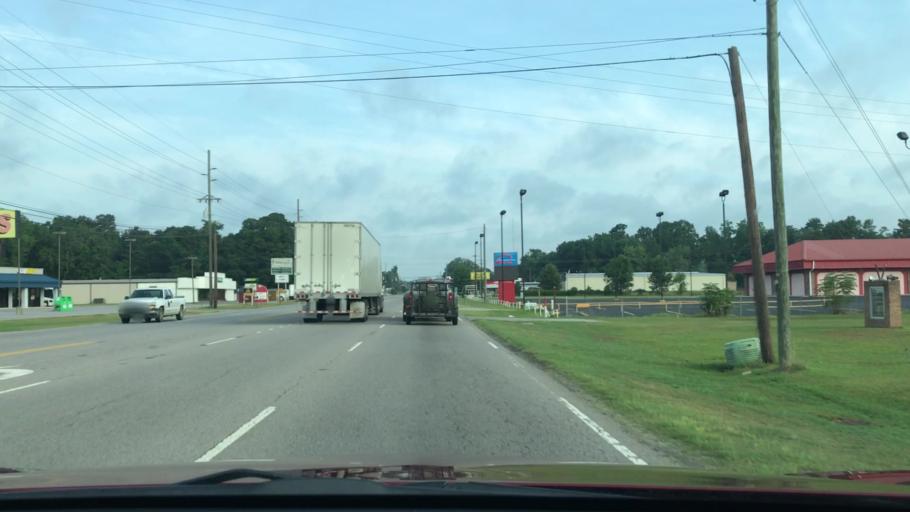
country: US
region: South Carolina
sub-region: Orangeburg County
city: Wilkinson Heights
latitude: 33.4803
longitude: -80.8219
